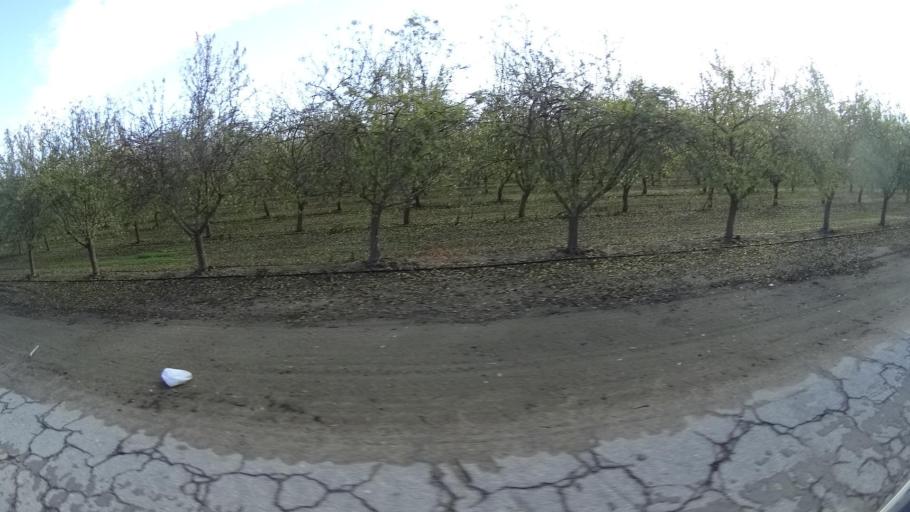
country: US
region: California
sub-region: Kern County
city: Delano
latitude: 35.7156
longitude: -119.3208
